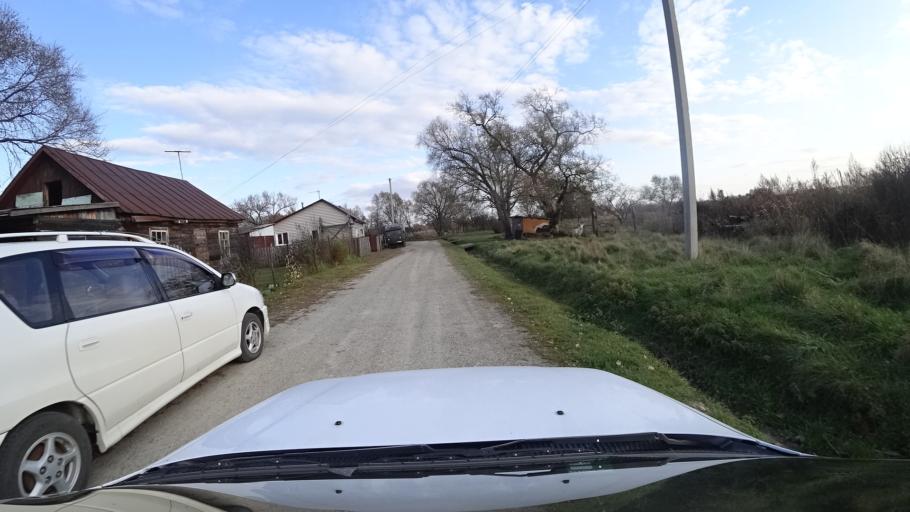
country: RU
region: Primorskiy
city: Lazo
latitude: 45.8217
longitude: 133.6161
